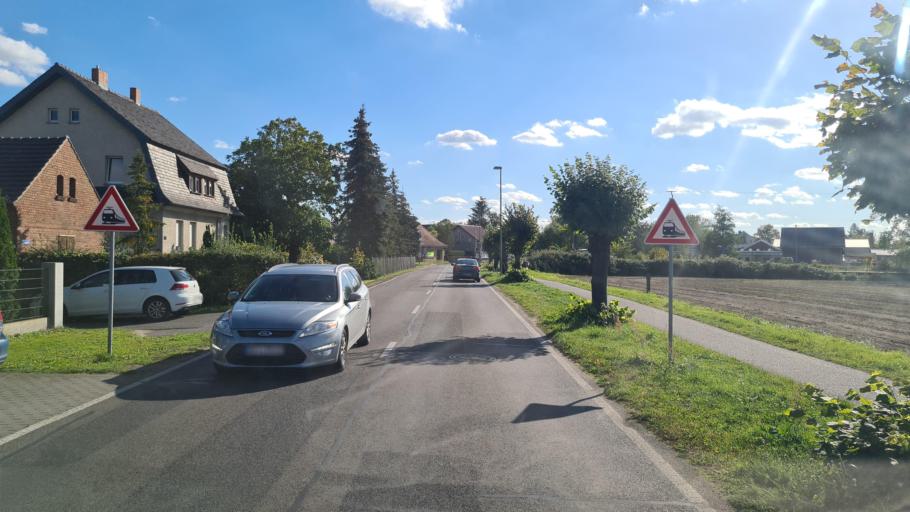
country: DE
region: Brandenburg
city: Kolkwitz
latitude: 51.7586
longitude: 14.2508
